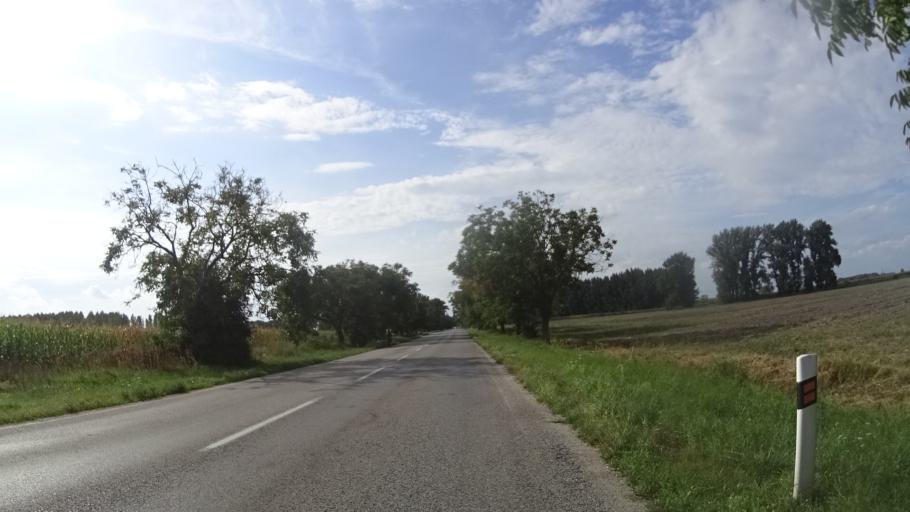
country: SK
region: Trnavsky
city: Gabcikovo
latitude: 47.9252
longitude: 17.4930
